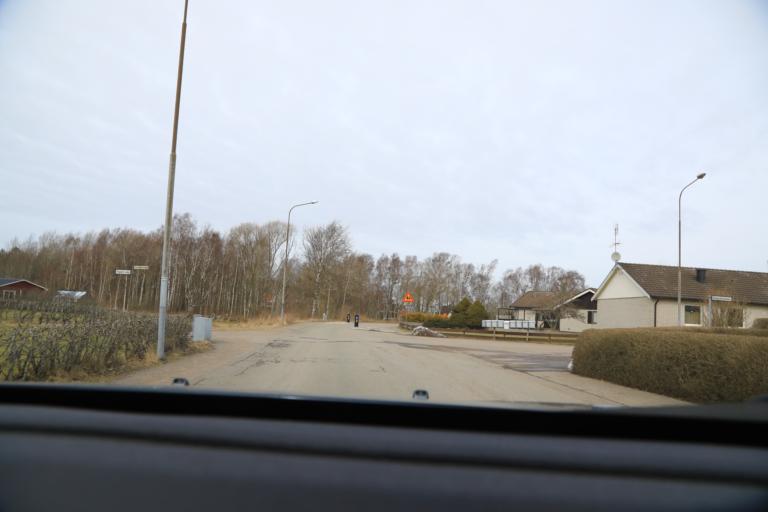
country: SE
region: Halland
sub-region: Kungsbacka Kommun
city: Frillesas
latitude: 57.2324
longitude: 12.1230
